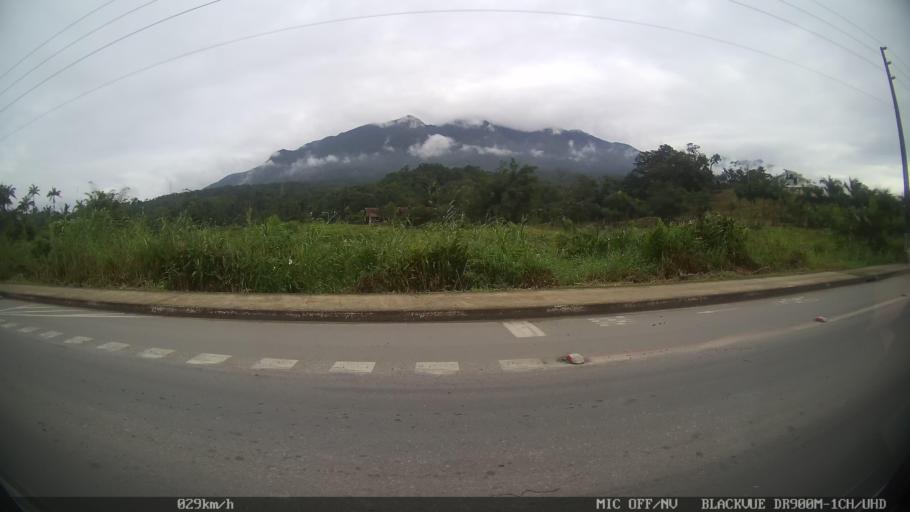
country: BR
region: Santa Catarina
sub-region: Joinville
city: Joinville
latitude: -26.0550
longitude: -48.8570
